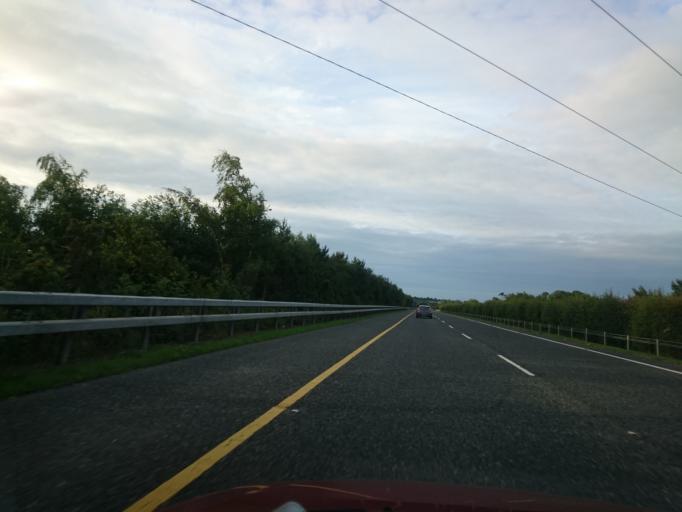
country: IE
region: Leinster
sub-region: Wicklow
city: Arklow
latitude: 52.7922
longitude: -6.1808
